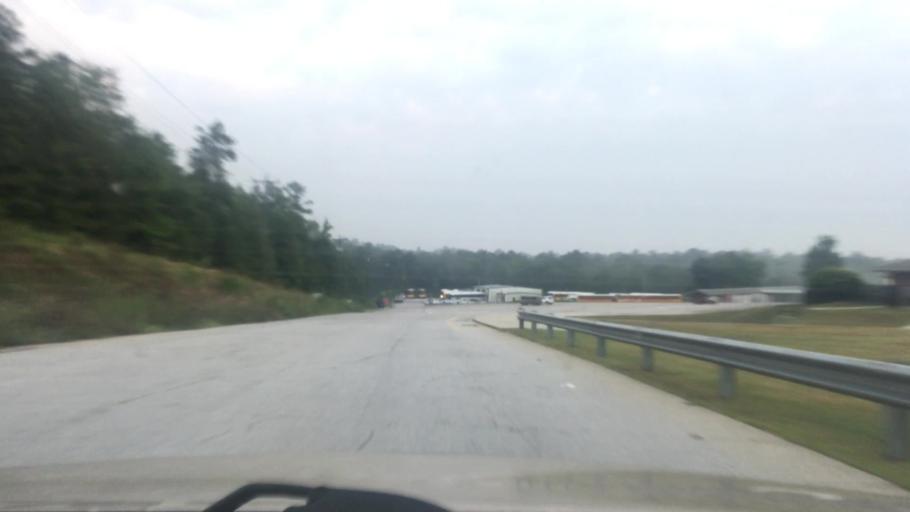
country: US
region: South Carolina
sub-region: Richland County
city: Lake Murray of Richland
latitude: 34.1513
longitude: -81.2049
